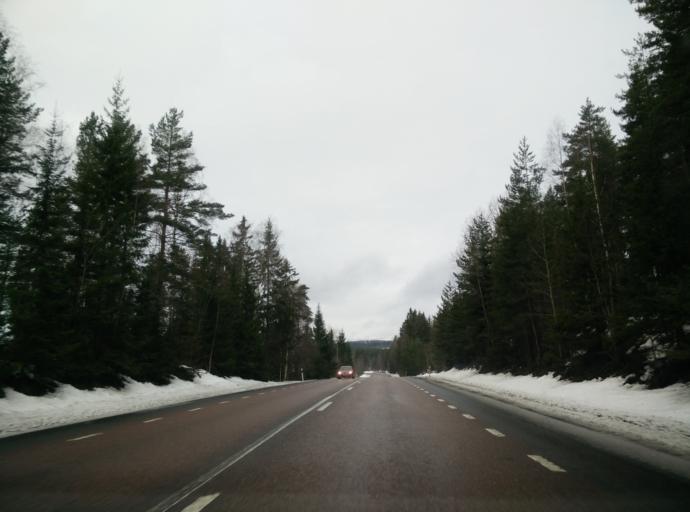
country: SE
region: Gaevleborg
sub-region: Hofors Kommun
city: Hofors
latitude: 60.5641
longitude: 16.3780
